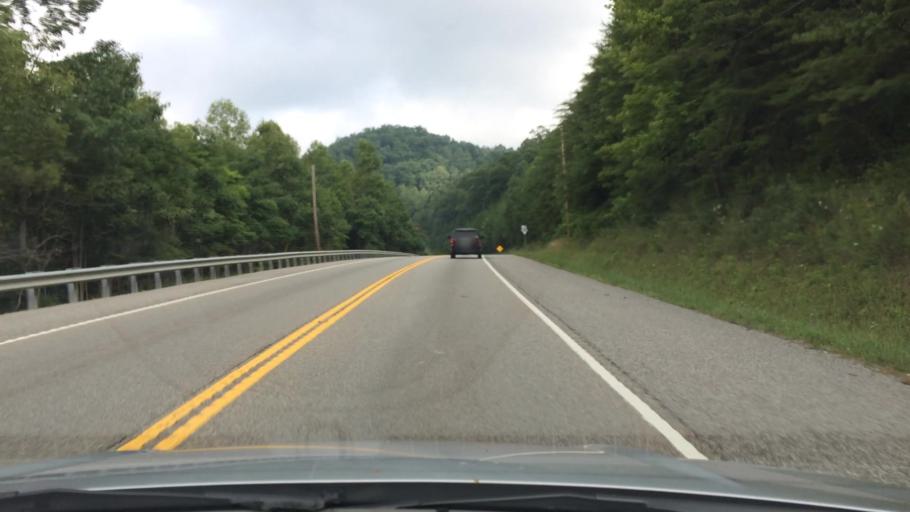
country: US
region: Tennessee
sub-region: Campbell County
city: Caryville
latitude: 36.4114
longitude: -84.2970
